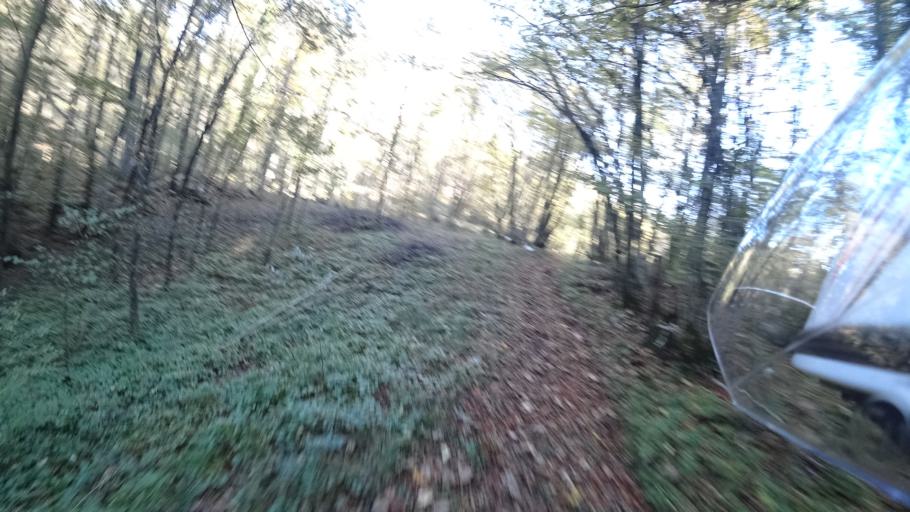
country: HR
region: Primorsko-Goranska
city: Matulji
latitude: 45.3837
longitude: 14.2990
